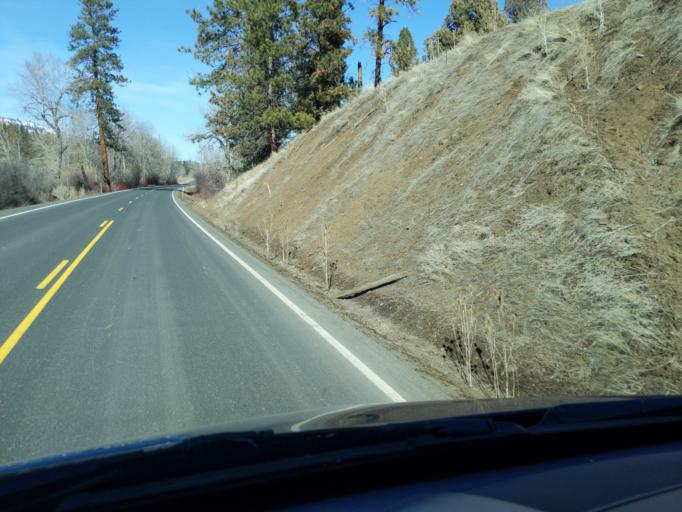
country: US
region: Oregon
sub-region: Grant County
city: John Day
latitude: 44.8528
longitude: -119.0302
